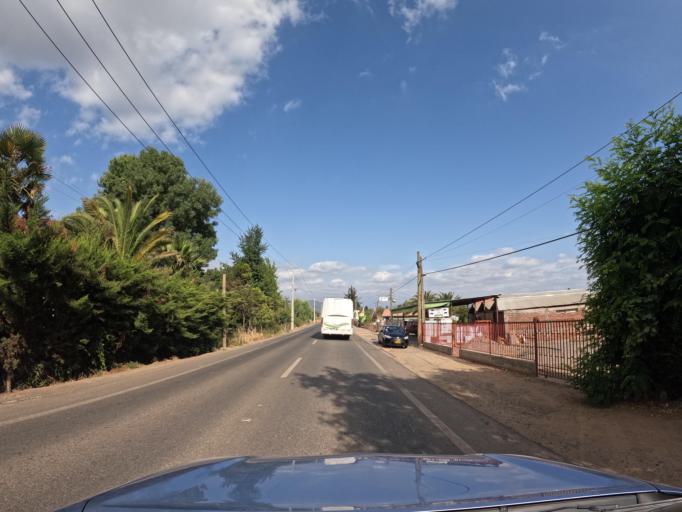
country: CL
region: Maule
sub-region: Provincia de Curico
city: Molina
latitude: -35.2750
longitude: -71.2925
